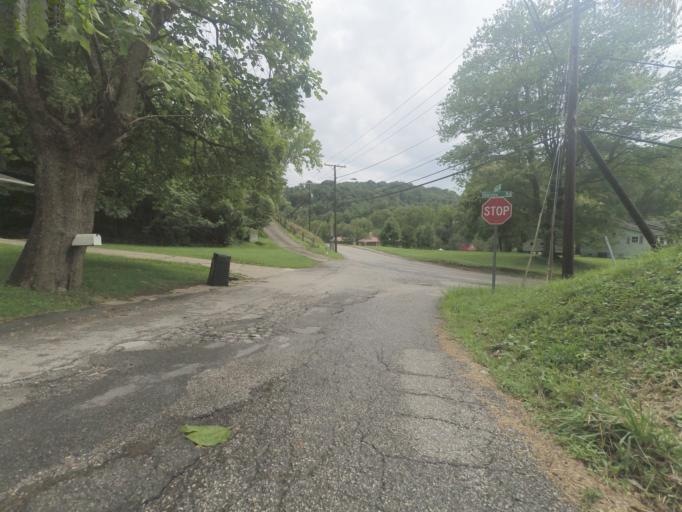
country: US
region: West Virginia
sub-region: Cabell County
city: Huntington
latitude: 38.4004
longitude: -82.4728
